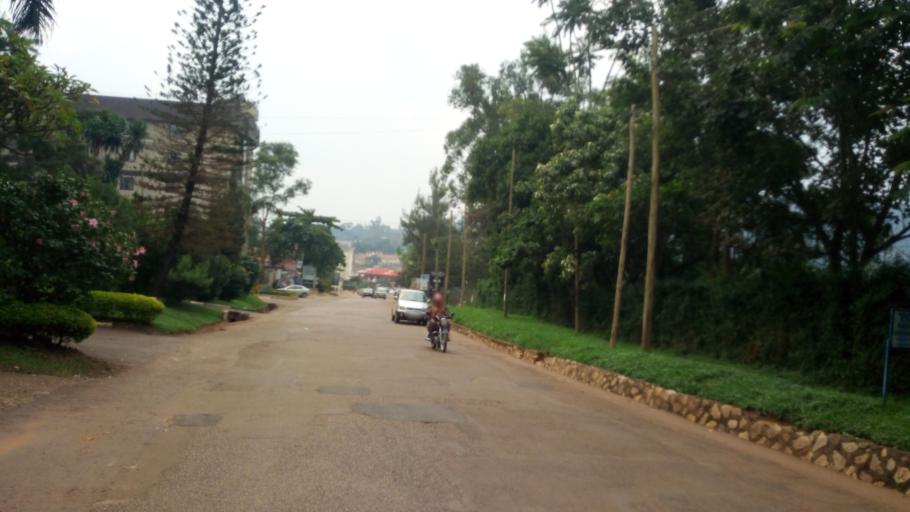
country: UG
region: Central Region
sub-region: Wakiso District
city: Kireka
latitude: 0.3153
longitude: 32.6234
